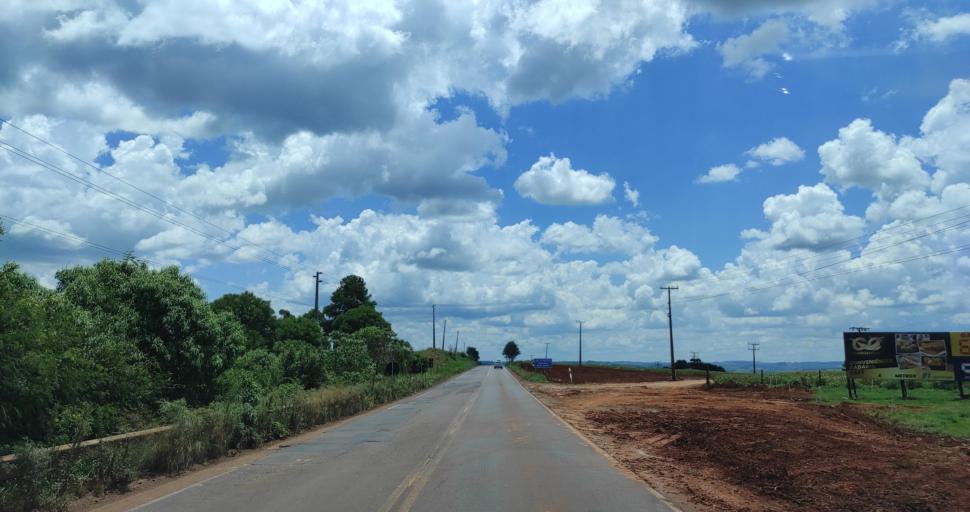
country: BR
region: Santa Catarina
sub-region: Xanxere
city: Xanxere
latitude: -26.7828
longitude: -52.4077
